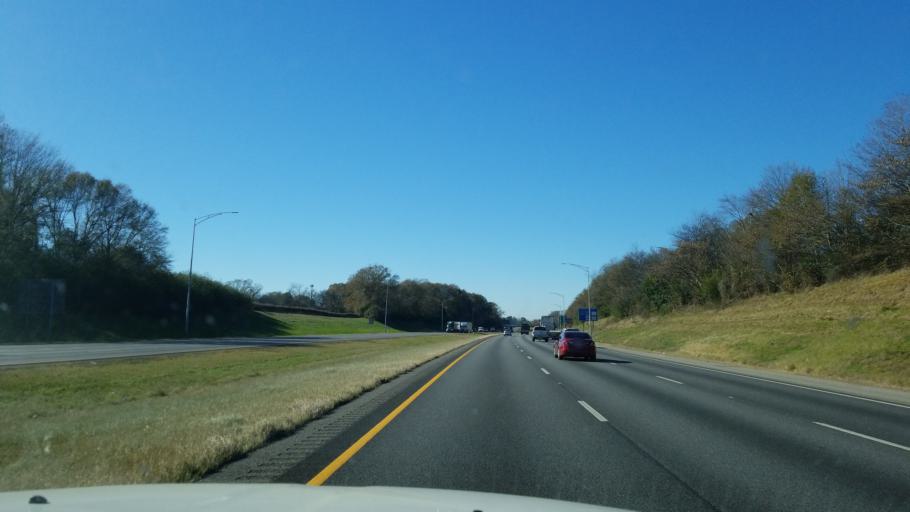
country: US
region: Alabama
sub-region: Tuscaloosa County
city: Tuscaloosa
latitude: 33.1705
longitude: -87.5362
